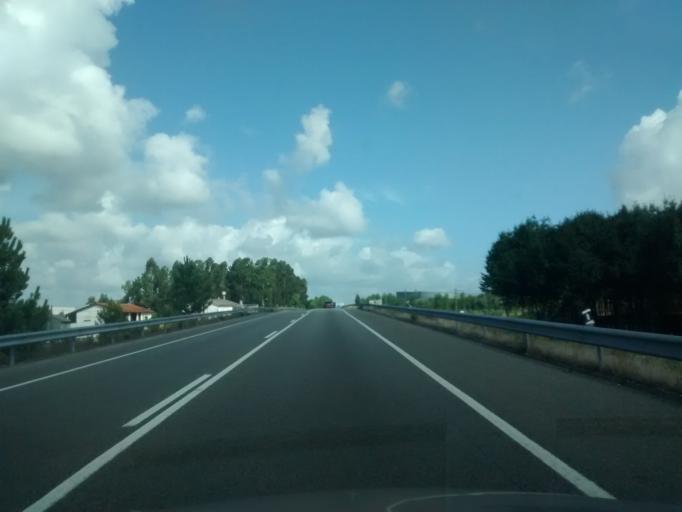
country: PT
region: Aveiro
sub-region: Anadia
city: Sangalhos
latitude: 40.4743
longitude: -8.4724
